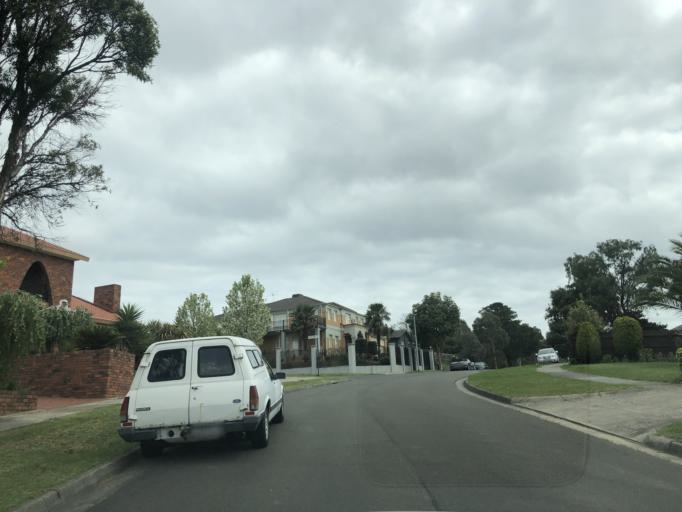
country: AU
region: Victoria
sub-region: Monash
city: Mulgrave
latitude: -37.9290
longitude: 145.2025
